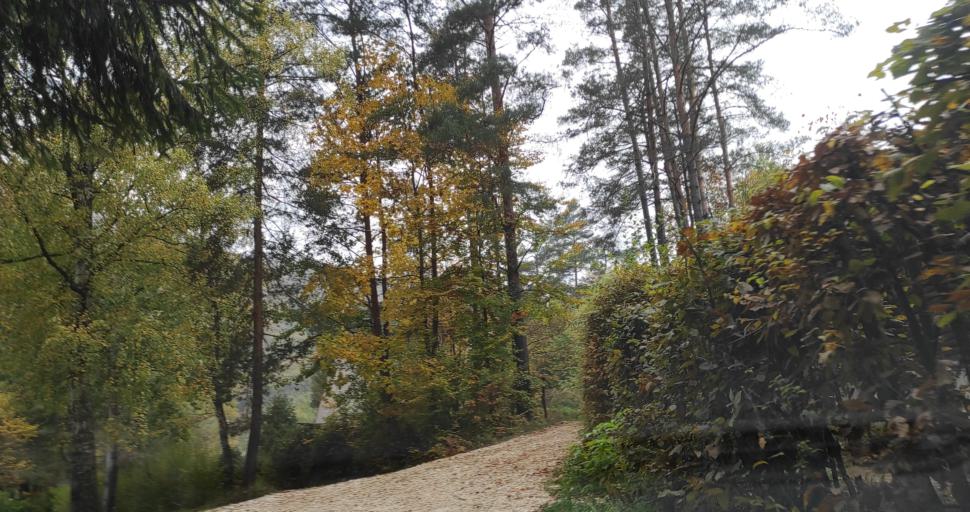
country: SK
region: Kosicky
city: Gelnica
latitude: 48.8830
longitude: 21.0458
